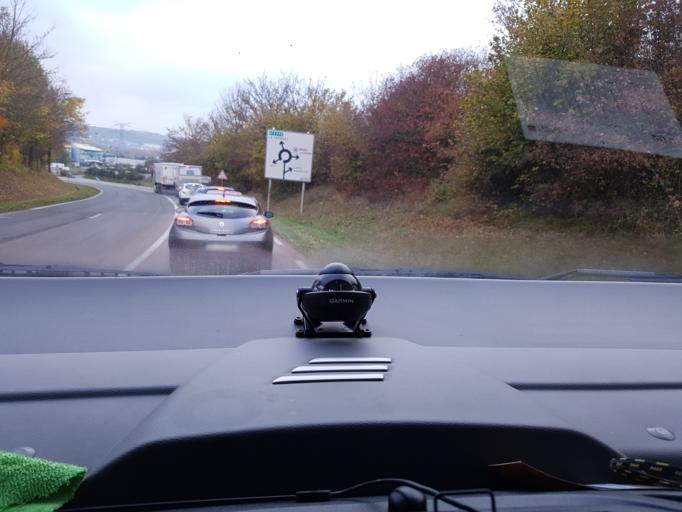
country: FR
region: Haute-Normandie
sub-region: Departement de la Seine-Maritime
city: Eu
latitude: 50.0612
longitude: 1.4121
